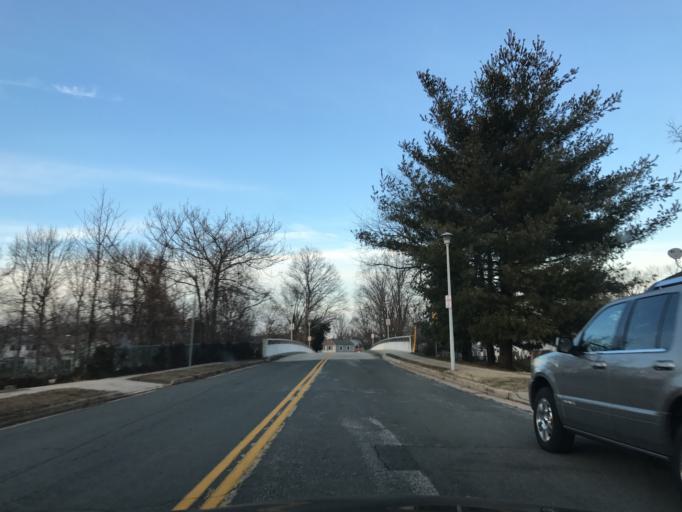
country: US
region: Maryland
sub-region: Harford County
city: Joppatowne
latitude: 39.4102
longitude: -76.3608
